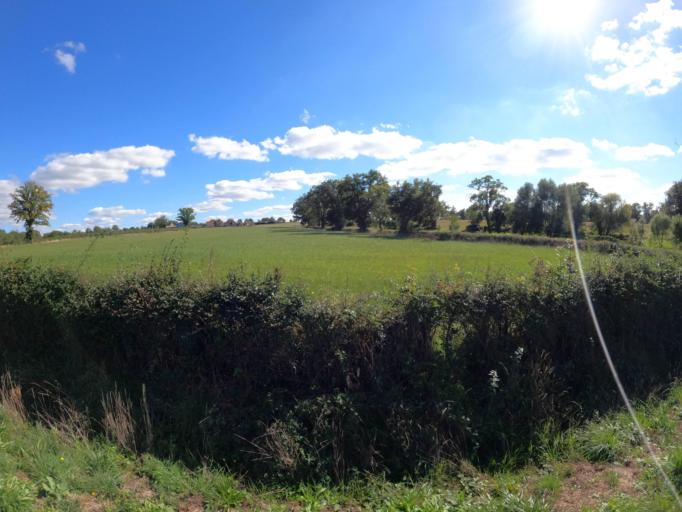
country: FR
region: Auvergne
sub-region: Departement de l'Allier
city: Buxieres-les-Mines
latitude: 46.4023
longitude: 2.9491
